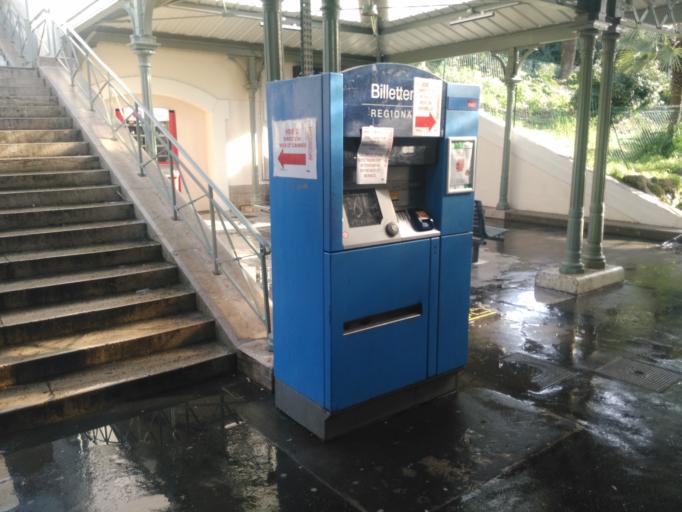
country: FR
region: Provence-Alpes-Cote d'Azur
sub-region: Departement des Alpes-Maritimes
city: Villefranche-sur-Mer
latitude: 43.7060
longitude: 7.2898
